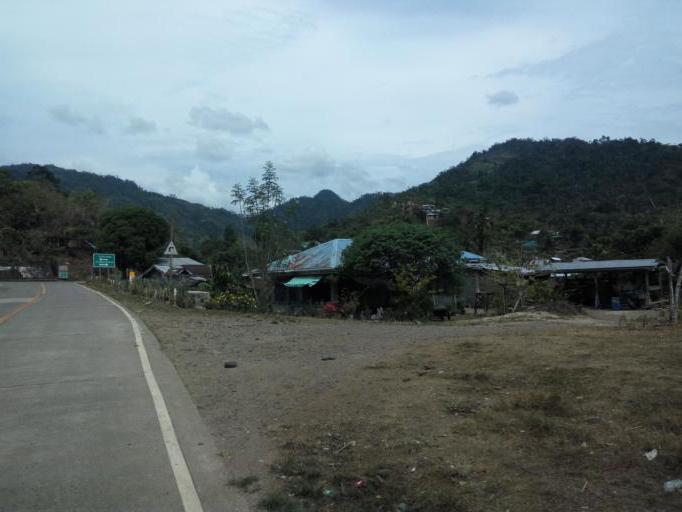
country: PH
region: Cagayan Valley
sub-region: Province of Quirino
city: Dumabato
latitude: 16.2558
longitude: 121.7181
